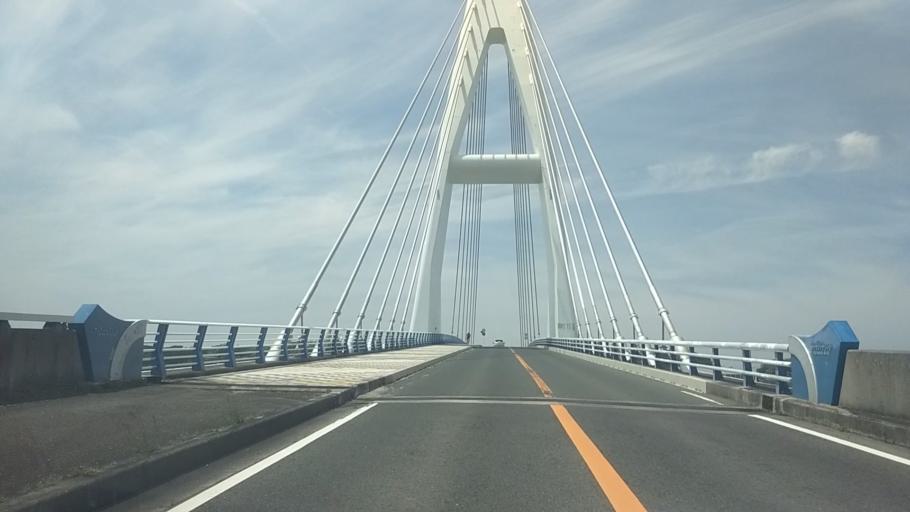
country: JP
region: Shizuoka
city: Kosai-shi
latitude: 34.6985
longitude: 137.5676
